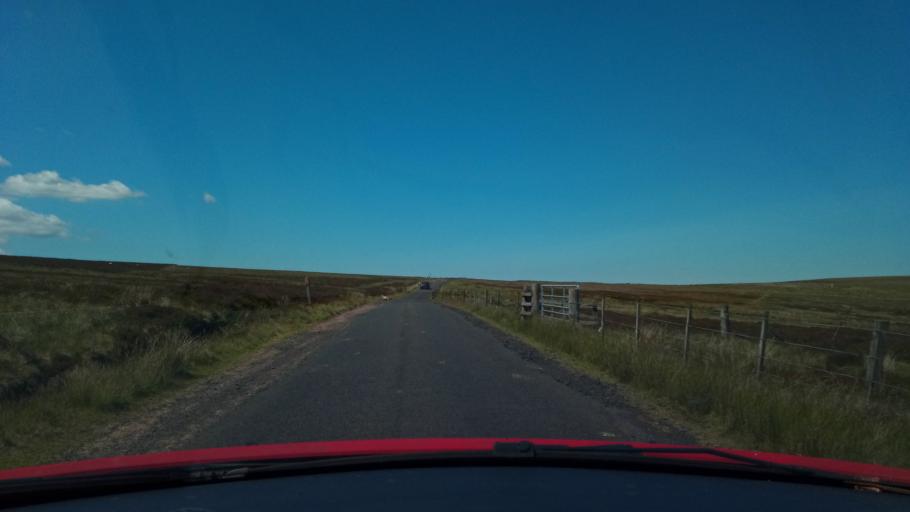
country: GB
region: Scotland
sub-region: East Lothian
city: Dunbar
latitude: 55.8390
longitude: -2.5547
